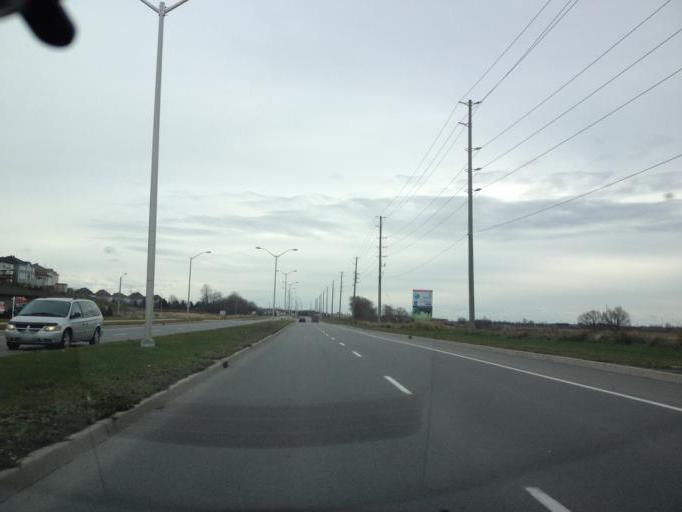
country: CA
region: Ontario
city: Bells Corners
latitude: 45.3131
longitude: -75.9366
